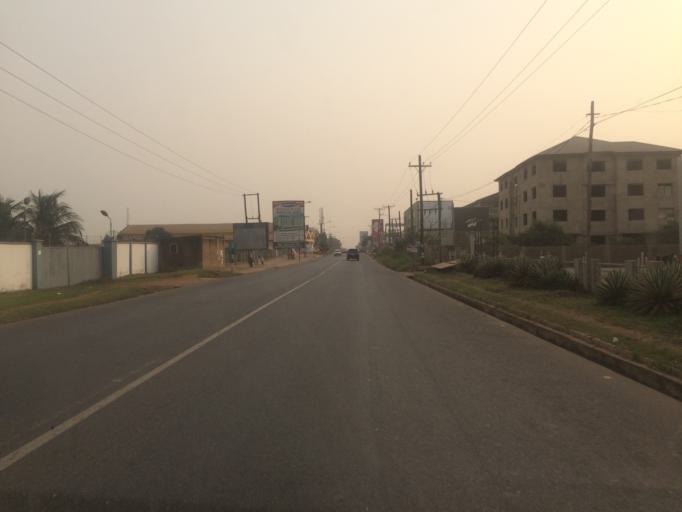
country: GH
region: Greater Accra
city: Medina Estates
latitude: 5.6411
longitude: -0.1177
